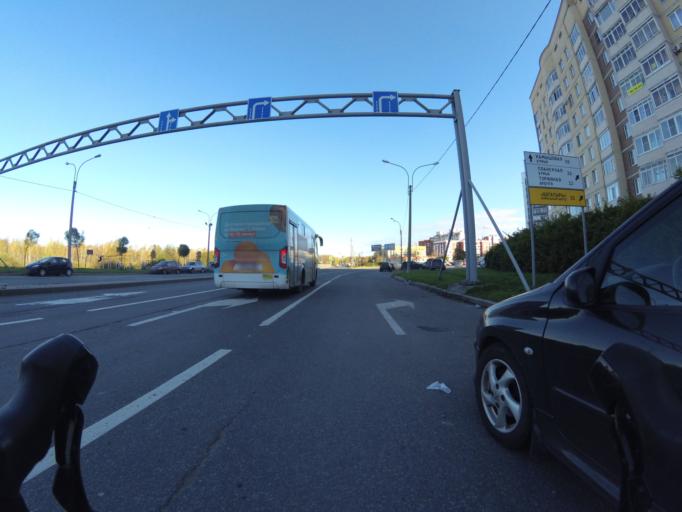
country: RU
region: Leningrad
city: Untolovo
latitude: 60.0082
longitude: 30.2011
